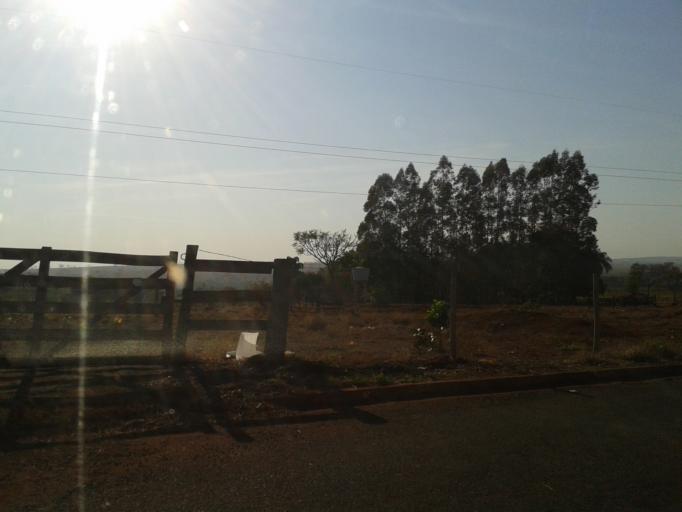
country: BR
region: Minas Gerais
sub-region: Ituiutaba
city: Ituiutaba
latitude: -18.9826
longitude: -49.4286
